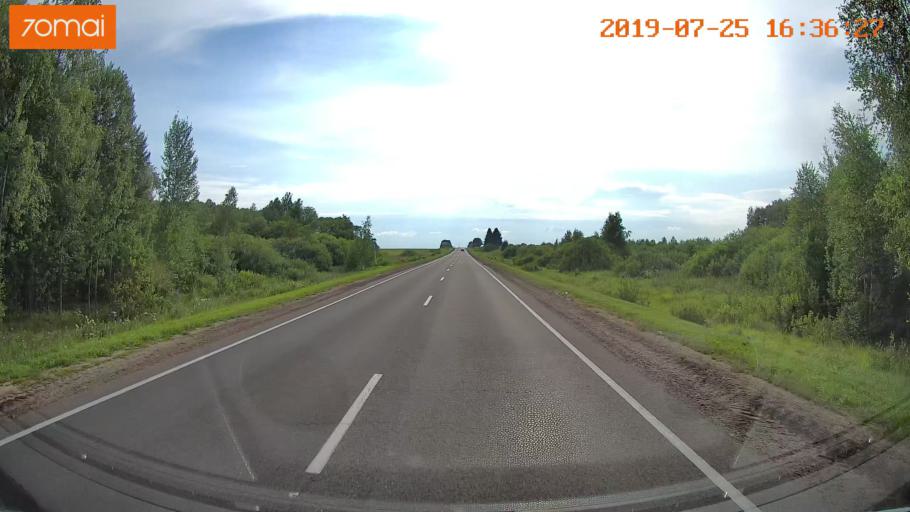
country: RU
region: Ivanovo
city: Privolzhsk
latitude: 57.3961
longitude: 41.4018
